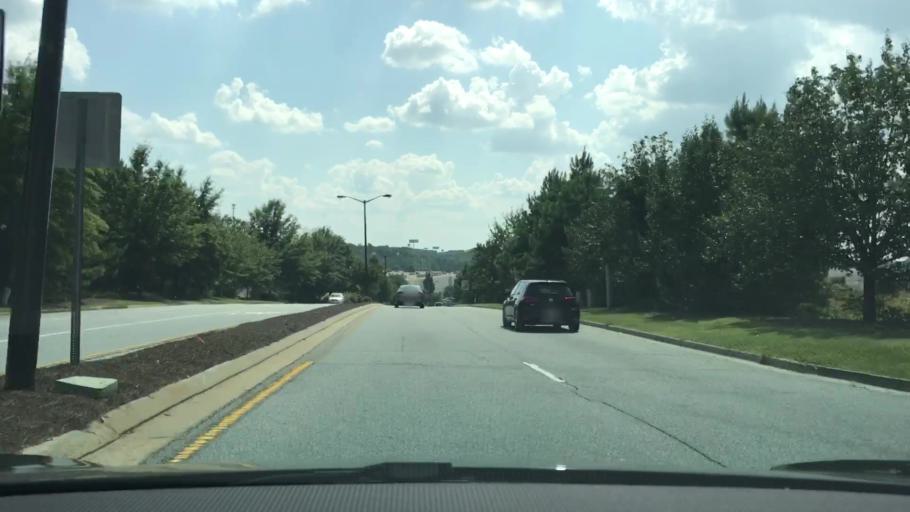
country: US
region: Georgia
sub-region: Gwinnett County
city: Suwanee
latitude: 34.0417
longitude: -84.0376
